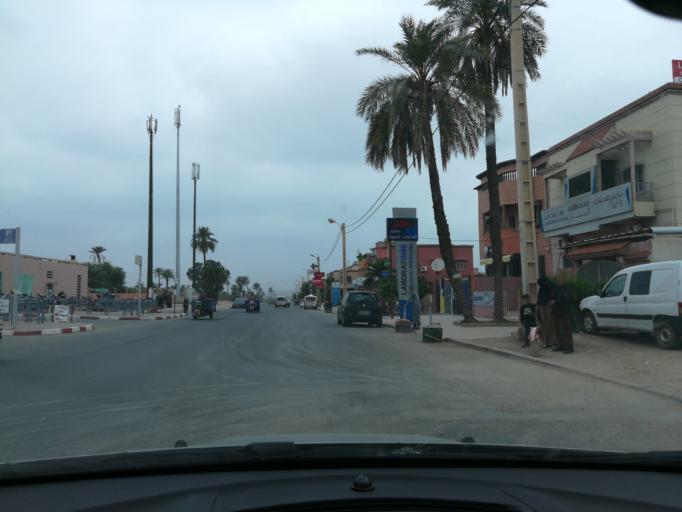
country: MA
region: Marrakech-Tensift-Al Haouz
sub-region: Marrakech
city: Marrakesh
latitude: 31.6650
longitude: -7.9947
